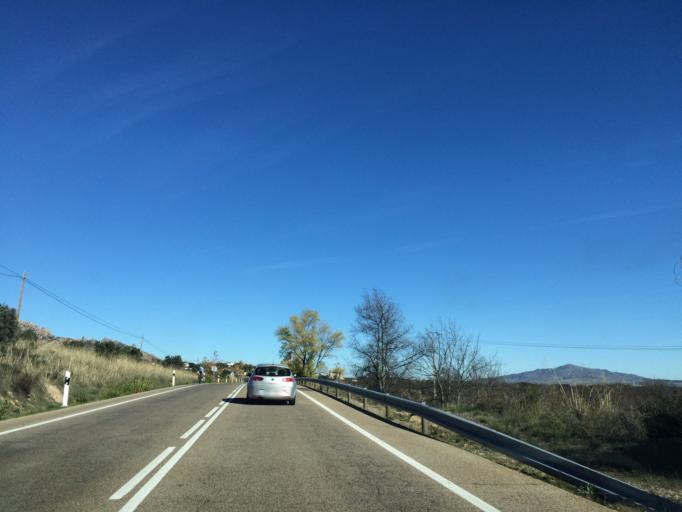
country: ES
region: Madrid
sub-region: Provincia de Madrid
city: Manzanares el Real
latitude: 40.7194
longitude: -3.8832
